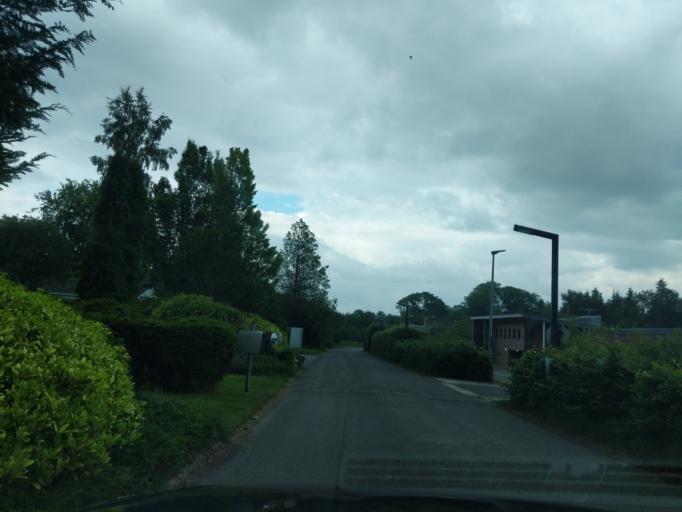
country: GB
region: Scotland
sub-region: Midlothian
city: Penicuik
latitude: 55.8596
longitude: -3.2097
